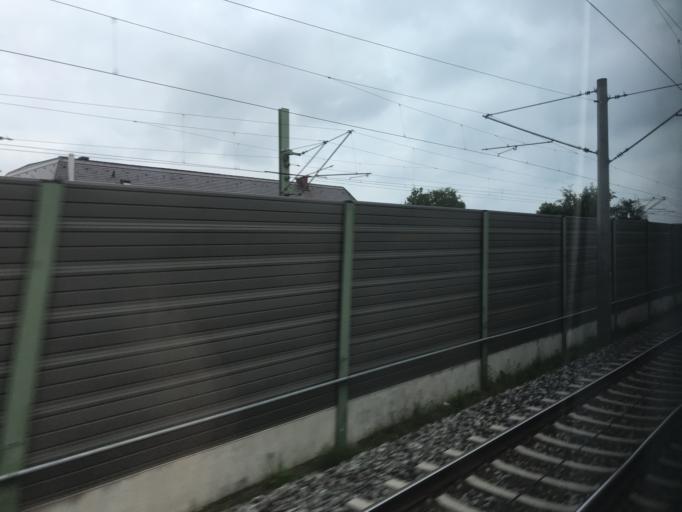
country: DE
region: Bavaria
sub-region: Swabia
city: Mering
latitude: 48.2636
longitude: 10.9870
